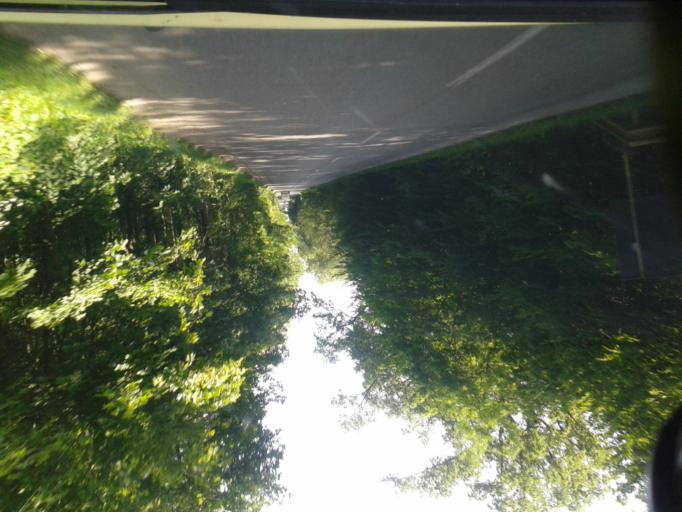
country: RO
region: Prahova
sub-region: Comuna Paulesti
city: Gageni
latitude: 45.0417
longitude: 25.9436
